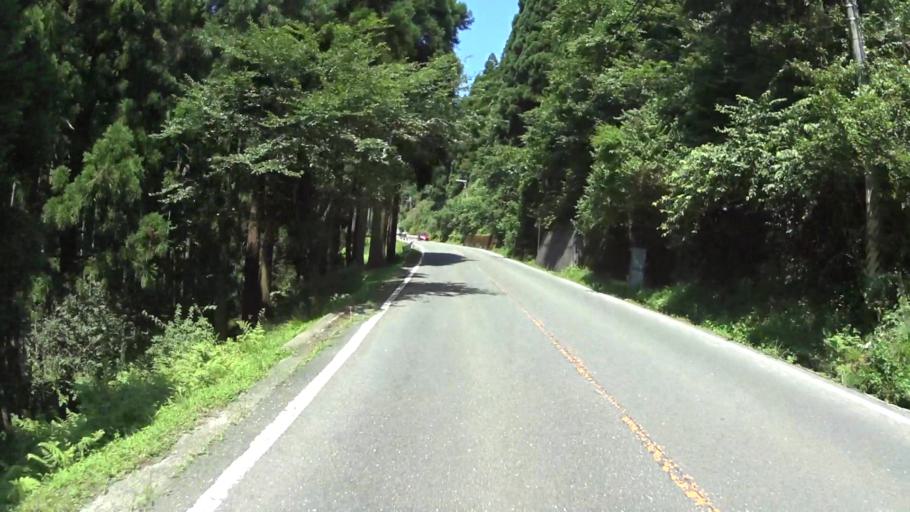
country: JP
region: Fukui
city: Obama
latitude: 35.3809
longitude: 135.9240
